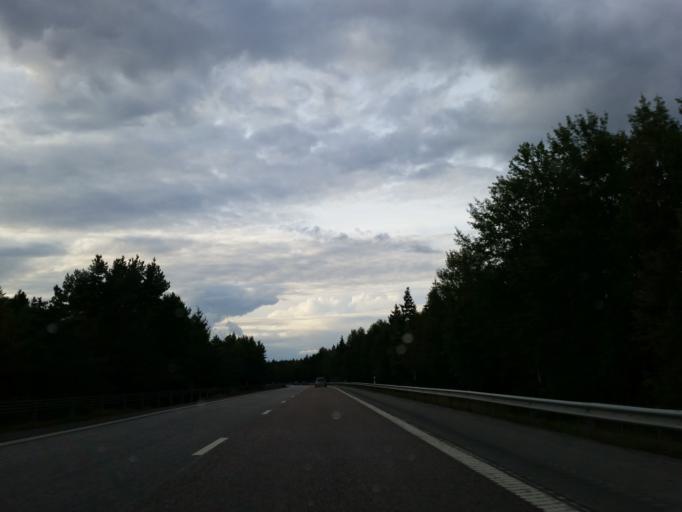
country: SE
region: Uppsala
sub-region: Knivsta Kommun
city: Knivsta
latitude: 59.7548
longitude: 17.8072
